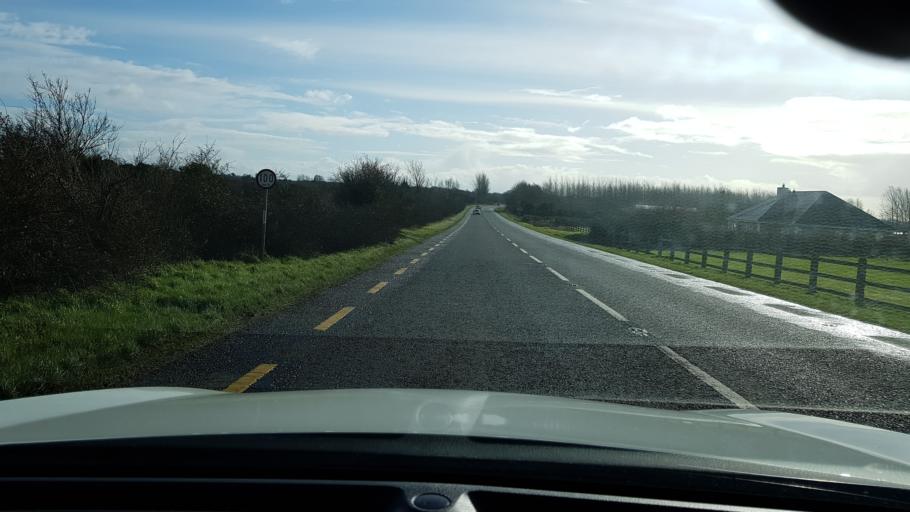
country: IE
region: Leinster
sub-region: An Longfort
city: Longford
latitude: 53.8020
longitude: -7.8776
